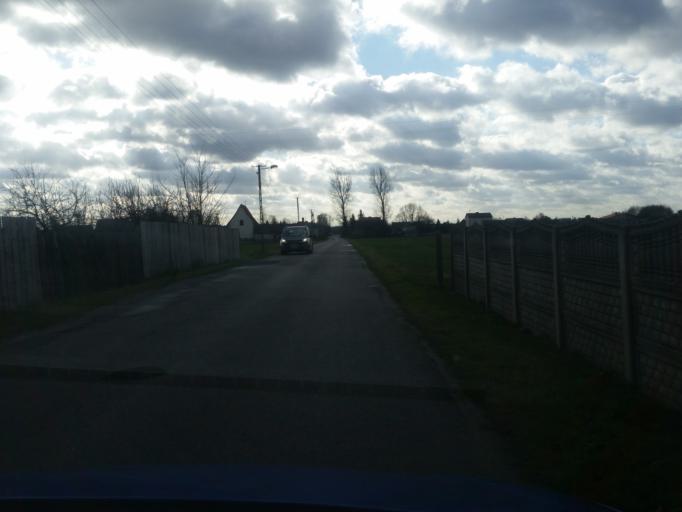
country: PL
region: Silesian Voivodeship
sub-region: Powiat czestochowski
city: Klomnice
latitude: 50.9645
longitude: 19.3276
